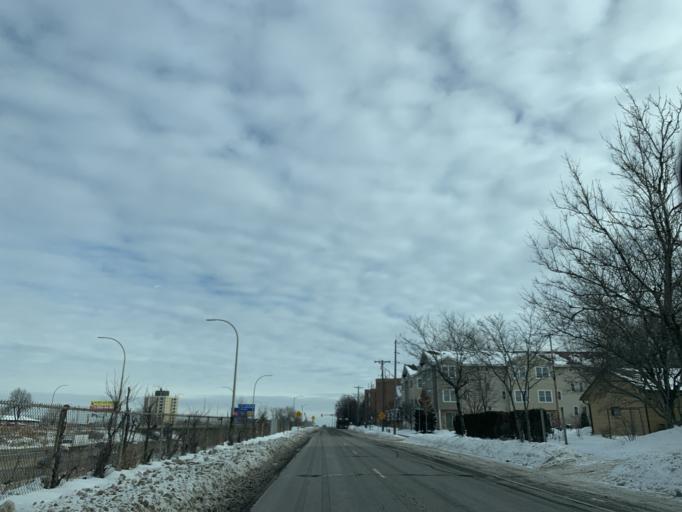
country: US
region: Minnesota
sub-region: Ramsey County
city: Saint Paul
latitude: 44.9513
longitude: -93.1297
